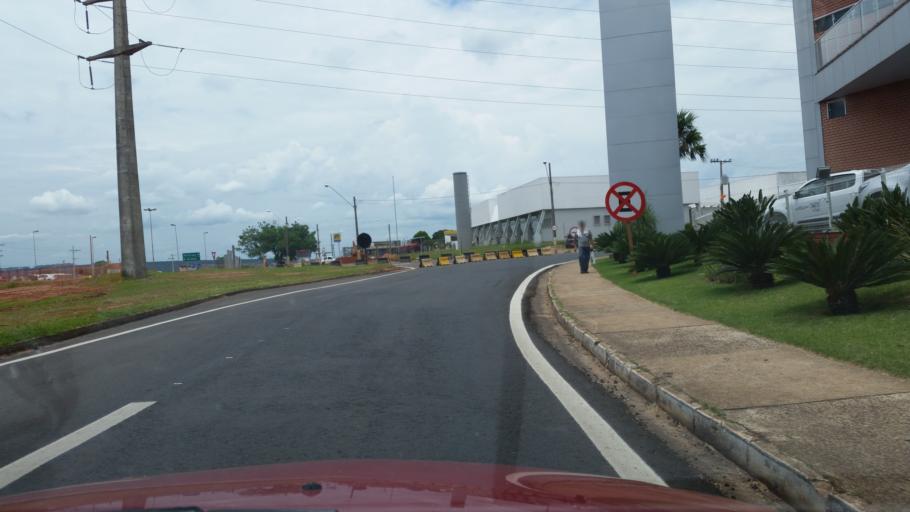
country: BR
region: Sao Paulo
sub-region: Avare
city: Avare
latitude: -23.0778
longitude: -48.9281
